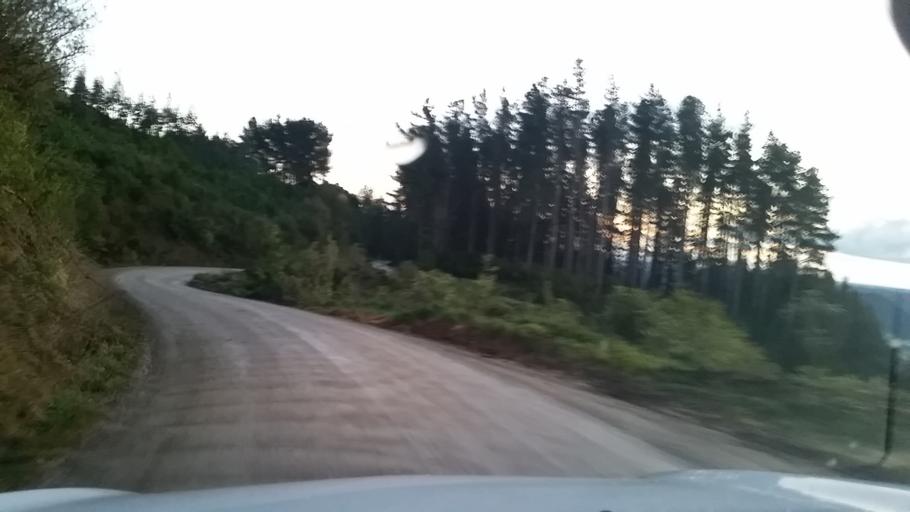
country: NZ
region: Manawatu-Wanganui
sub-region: Wanganui District
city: Wanganui
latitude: -39.7738
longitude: 174.8618
